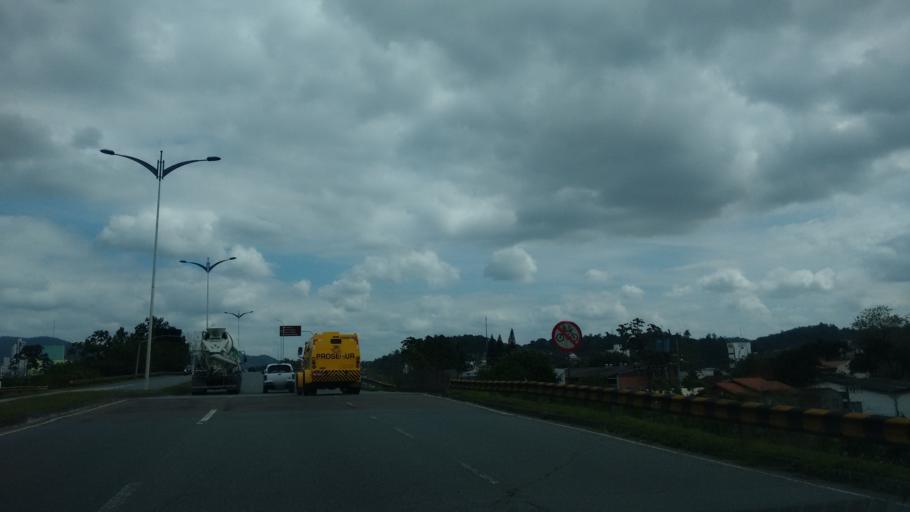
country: BR
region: Santa Catarina
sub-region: Blumenau
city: Blumenau
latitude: -26.8949
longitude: -49.0734
